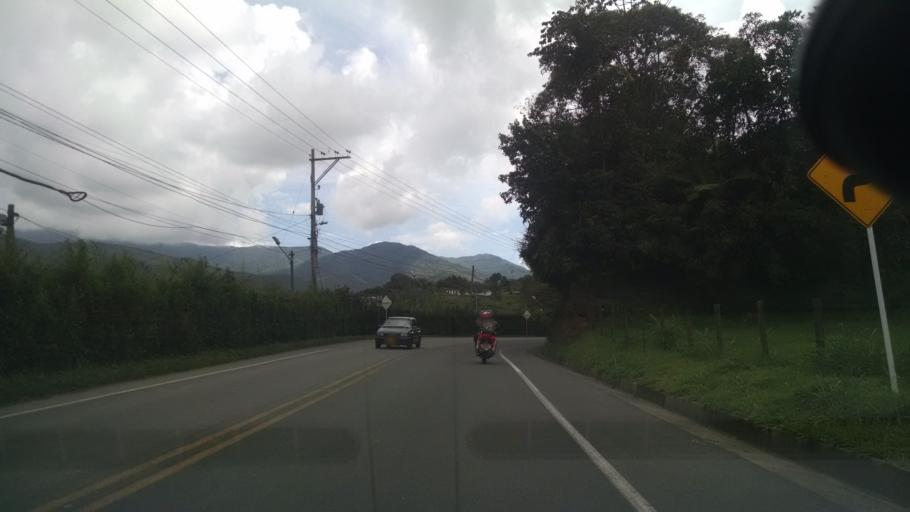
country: CO
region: Antioquia
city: Caldas
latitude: 6.0621
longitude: -75.6322
